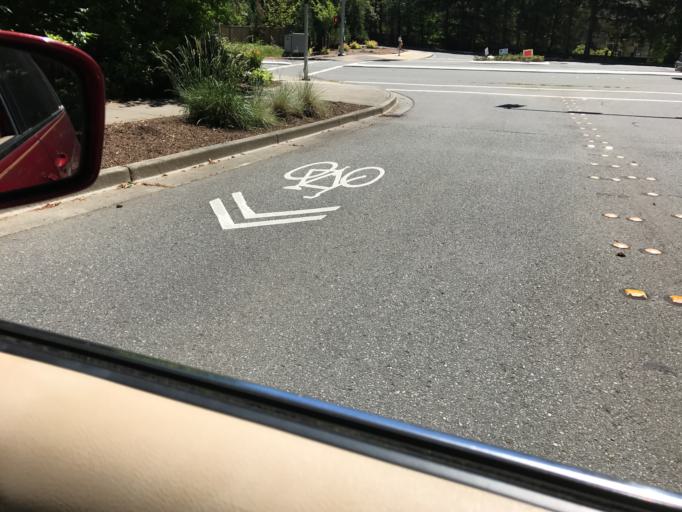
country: US
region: Washington
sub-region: King County
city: Redmond
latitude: 47.6373
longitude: -122.1252
